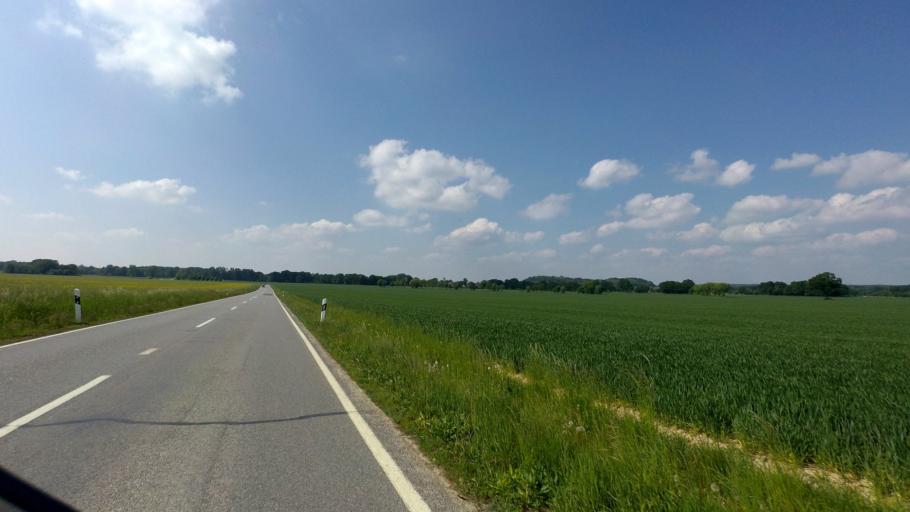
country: DE
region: Saxony
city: Weissenberg
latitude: 51.2155
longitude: 14.6025
